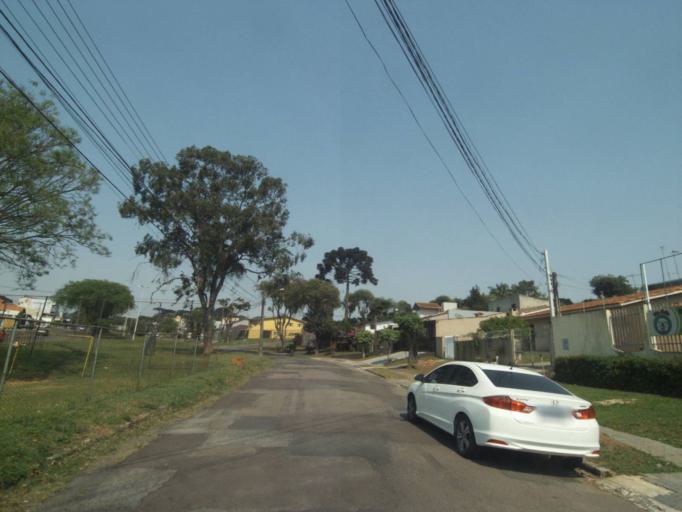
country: BR
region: Parana
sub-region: Sao Jose Dos Pinhais
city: Sao Jose dos Pinhais
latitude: -25.5248
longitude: -49.2498
